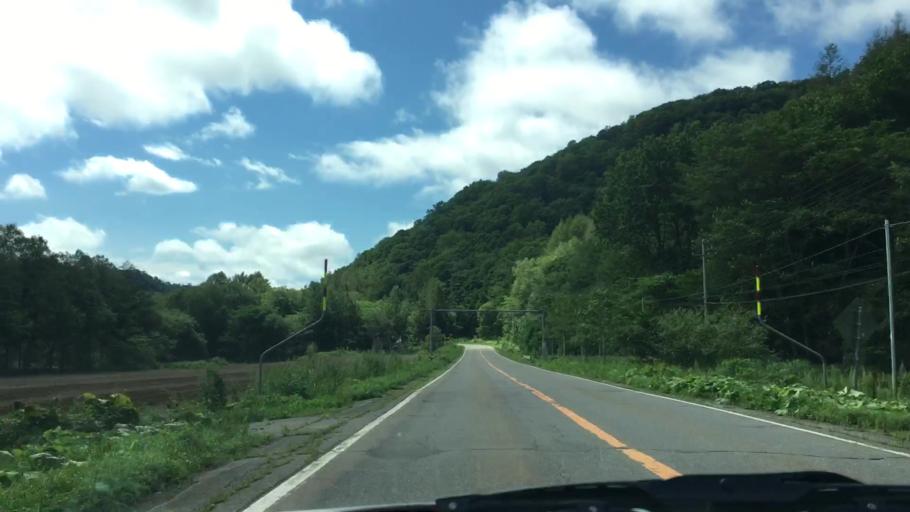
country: JP
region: Hokkaido
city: Kitami
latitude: 43.3521
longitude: 143.7798
